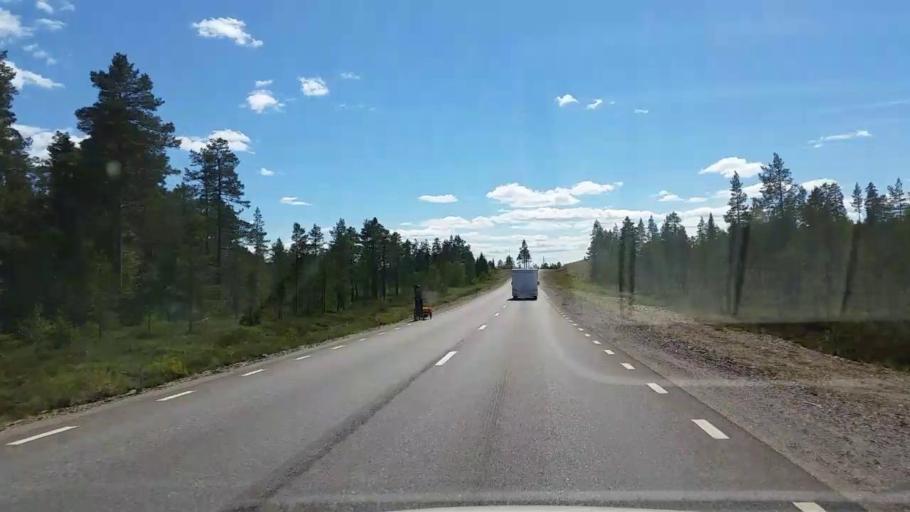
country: SE
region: Gaevleborg
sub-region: Bollnas Kommun
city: Vittsjo
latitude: 61.1053
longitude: 15.8580
